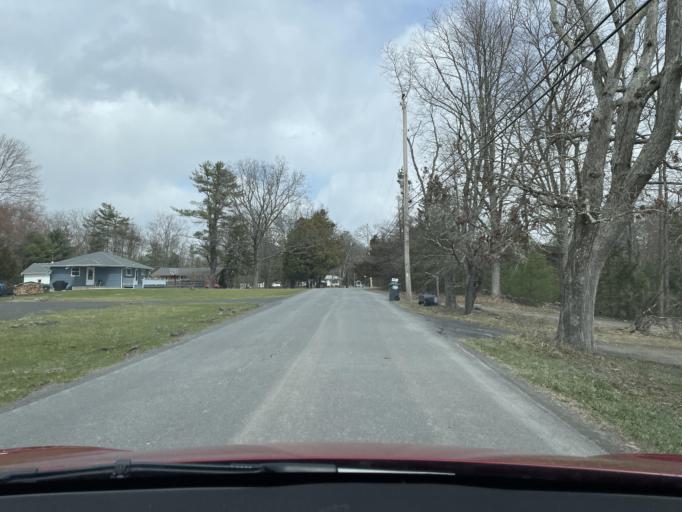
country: US
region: New York
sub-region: Ulster County
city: Zena
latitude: 42.0394
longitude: -74.0351
